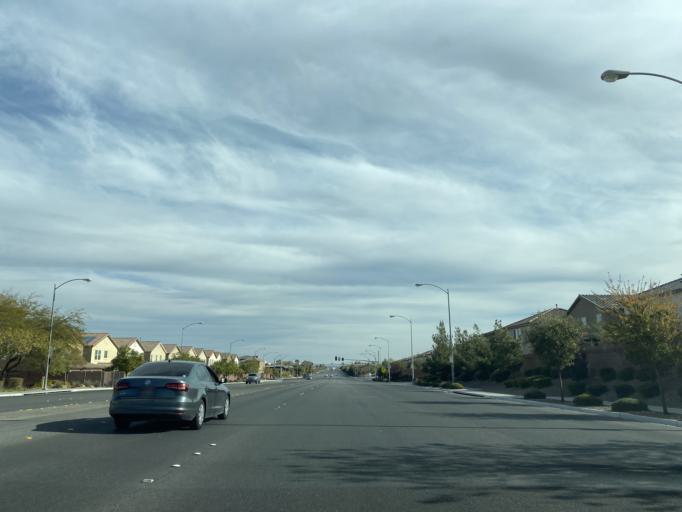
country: US
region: Nevada
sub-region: Clark County
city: Summerlin South
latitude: 36.0700
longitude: -115.3100
